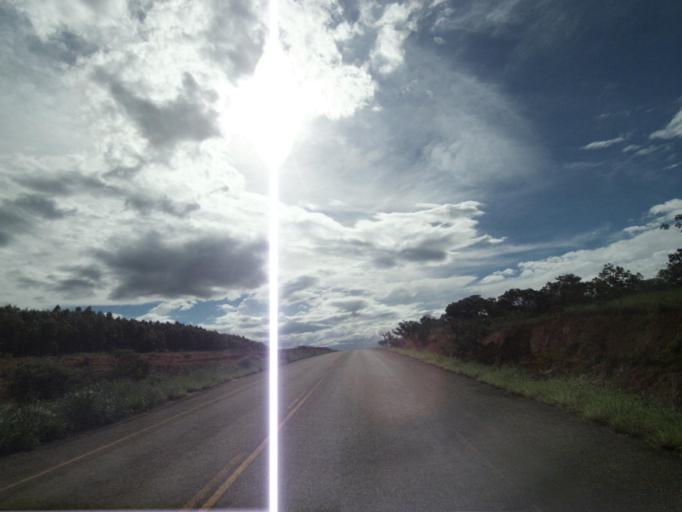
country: BR
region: Goias
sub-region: Jaragua
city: Jaragua
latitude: -15.8384
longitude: -49.3041
